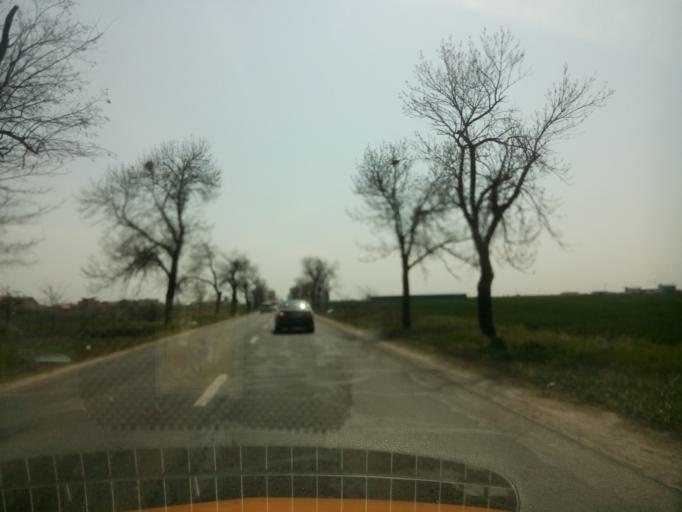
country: RO
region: Ilfov
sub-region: Comuna Glina
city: Glina
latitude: 44.3399
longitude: 26.2356
